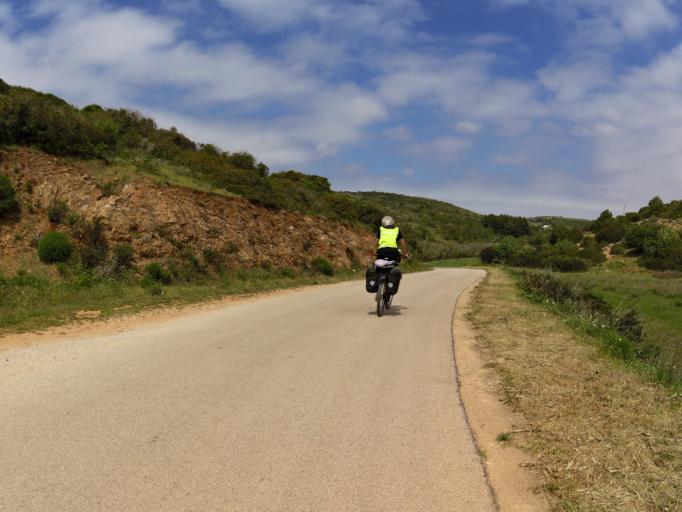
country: PT
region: Faro
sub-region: Vila do Bispo
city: Vila do Bispo
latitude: 37.0676
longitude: -8.8713
